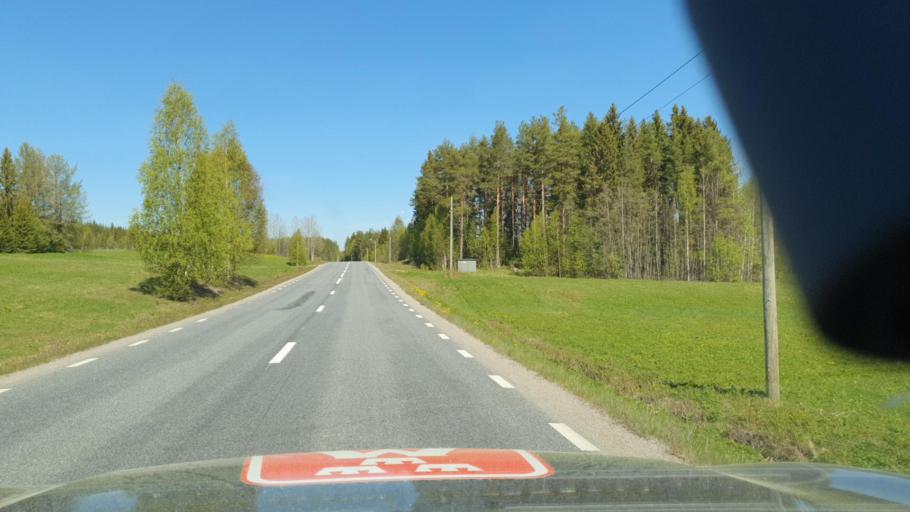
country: SE
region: Vaesternorrland
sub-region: OErnskoeldsviks Kommun
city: Bredbyn
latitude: 63.7244
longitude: 18.5006
